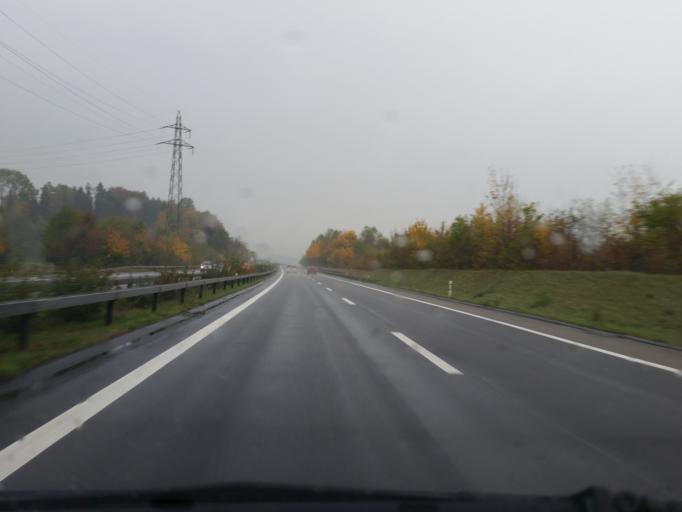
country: CH
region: Thurgau
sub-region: Frauenfeld District
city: Frauenfeld
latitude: 47.5617
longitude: 8.8725
